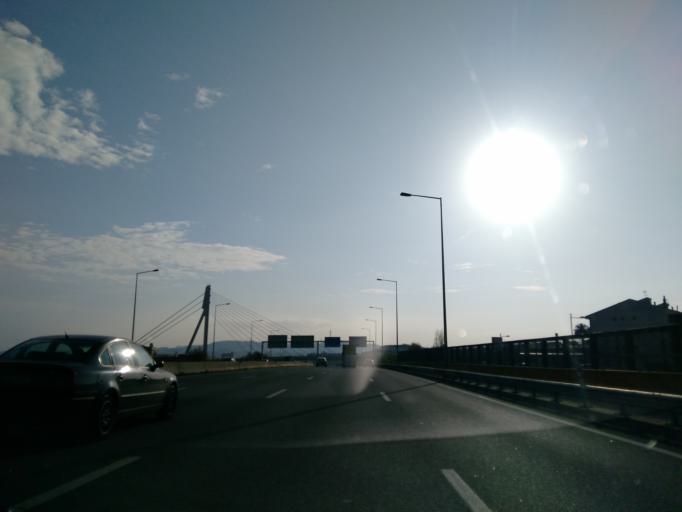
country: PT
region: Porto
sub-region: Porto
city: Porto
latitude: 41.1597
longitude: -8.5822
